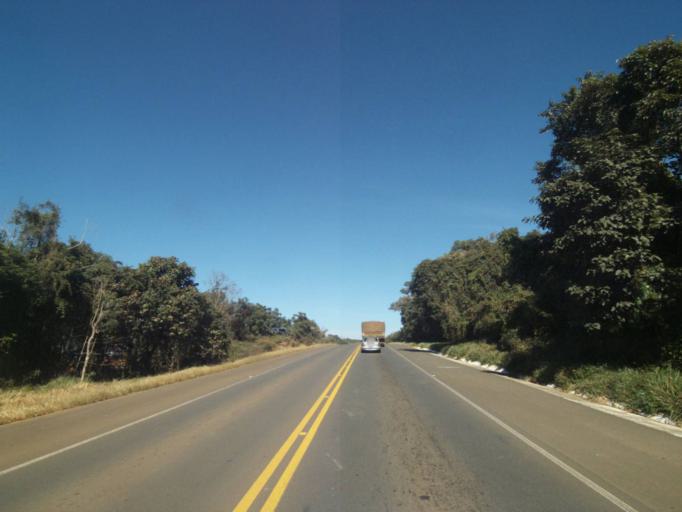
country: BR
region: Parana
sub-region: Tibagi
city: Tibagi
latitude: -24.7166
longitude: -50.4497
